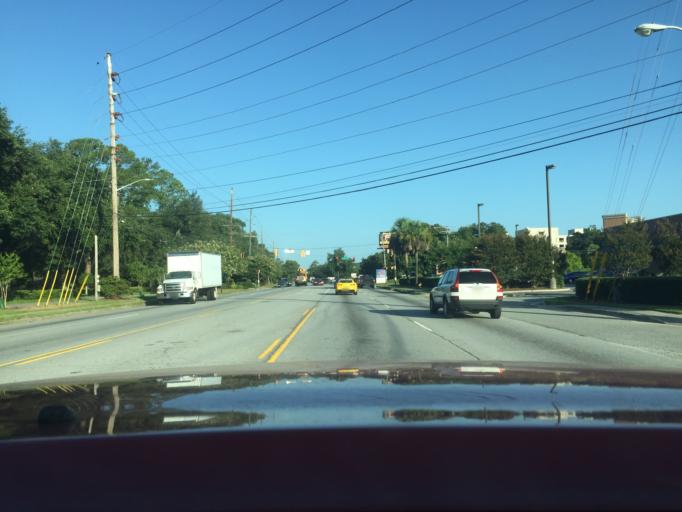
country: US
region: Georgia
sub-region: Chatham County
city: Thunderbolt
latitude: 32.0251
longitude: -81.0967
